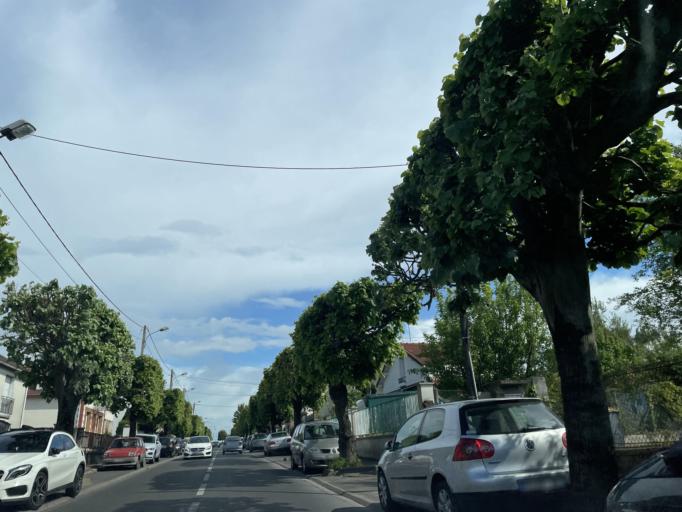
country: FR
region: Ile-de-France
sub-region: Departement du Val-d'Oise
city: Arnouville
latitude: 48.9849
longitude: 2.4163
